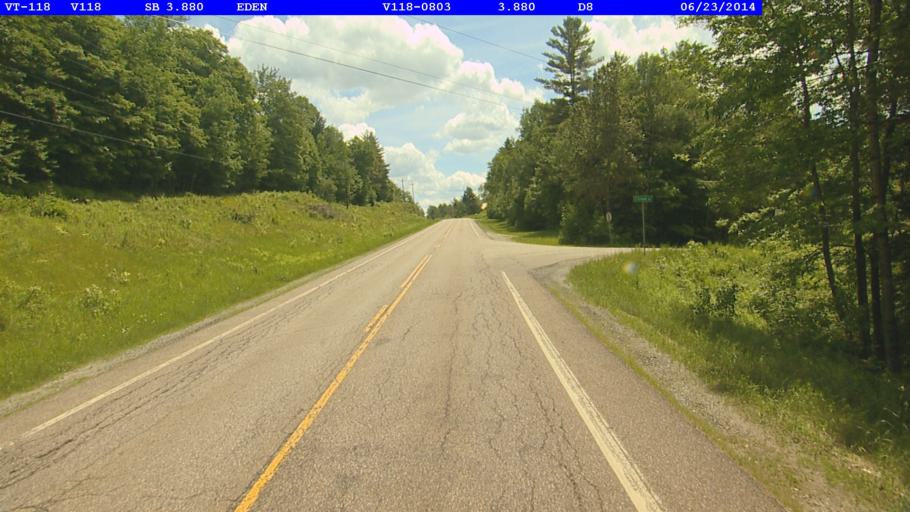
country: US
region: Vermont
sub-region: Lamoille County
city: Johnson
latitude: 44.7552
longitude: -72.5796
